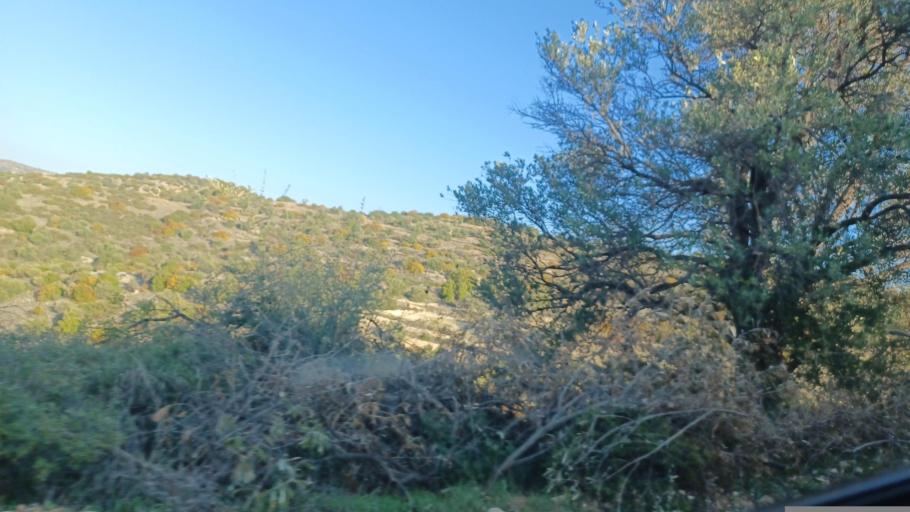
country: CY
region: Pafos
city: Mesogi
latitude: 34.8689
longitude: 32.5714
